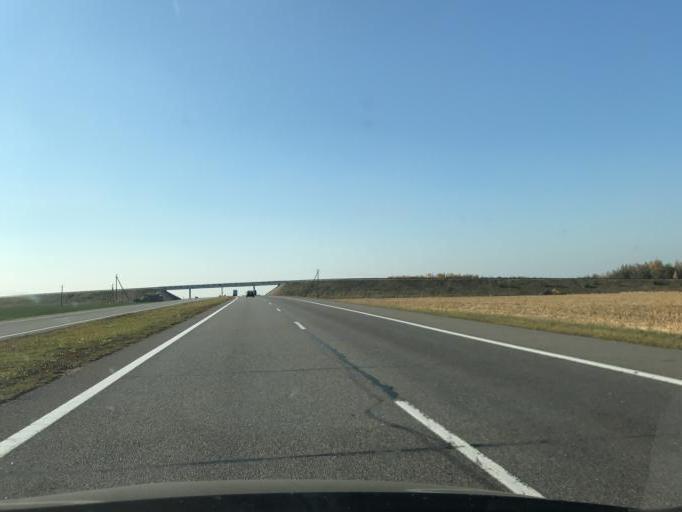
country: BY
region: Minsk
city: Stowbtsy
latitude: 53.5360
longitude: 26.8090
